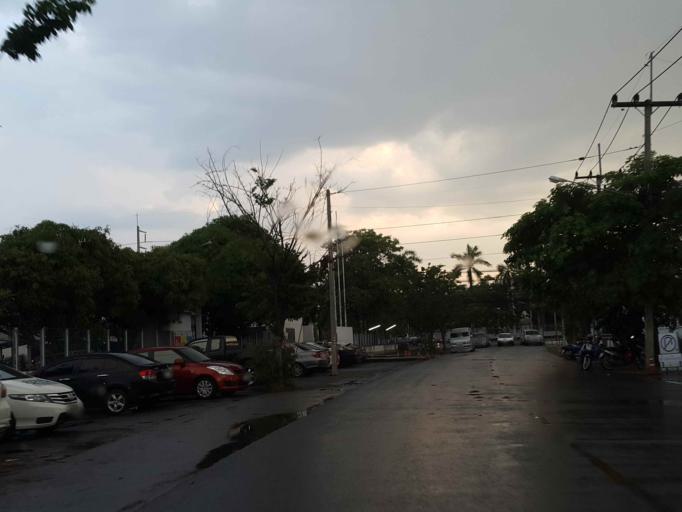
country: TH
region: Lamphun
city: Lamphun
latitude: 18.5906
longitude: 99.0496
